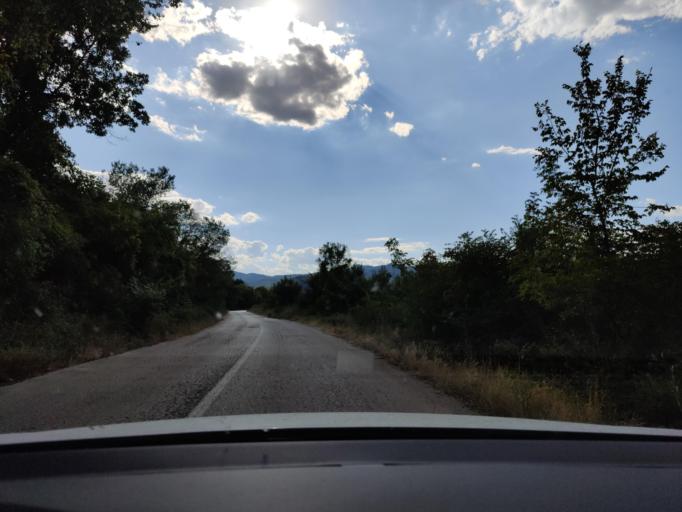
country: GR
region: Central Macedonia
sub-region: Nomos Serron
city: Chrysochorafa
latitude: 41.1767
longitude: 23.1200
